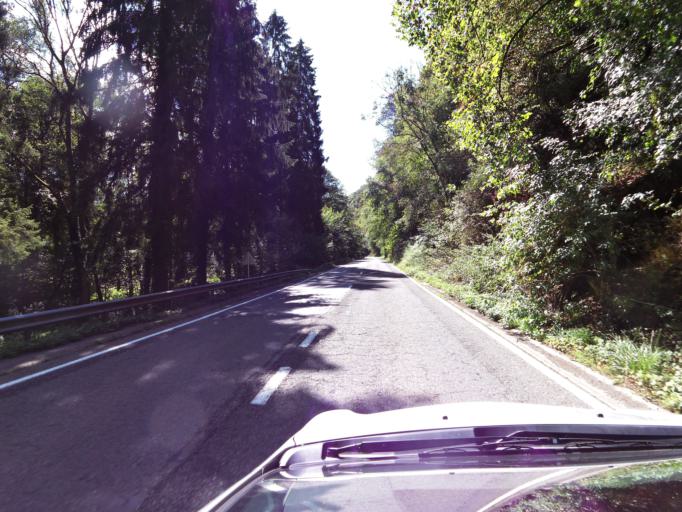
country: BE
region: Wallonia
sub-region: Province du Luxembourg
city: Rendeux
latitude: 50.2145
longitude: 5.5194
